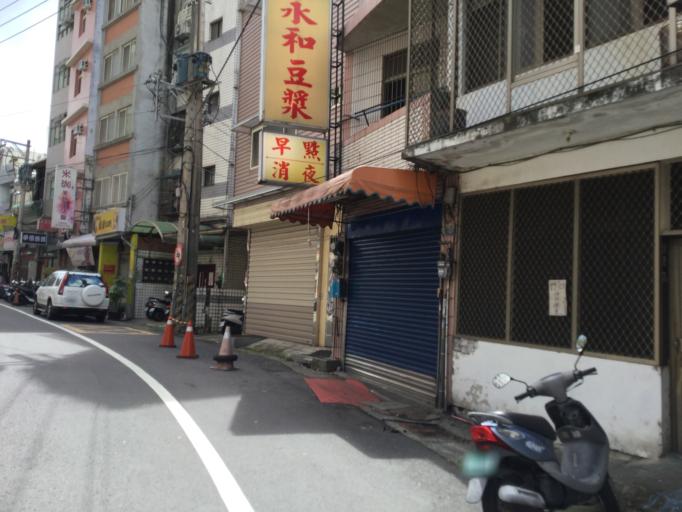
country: TW
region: Taiwan
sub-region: Hsinchu
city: Hsinchu
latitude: 24.7787
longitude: 121.0250
